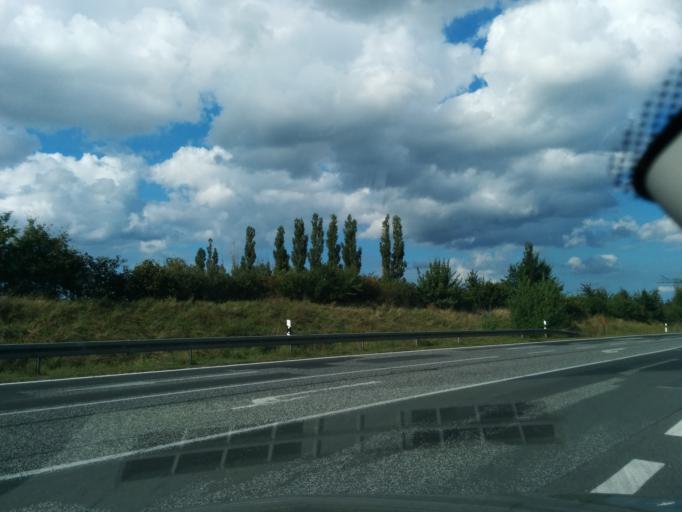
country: DE
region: Mecklenburg-Vorpommern
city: Pasewalk
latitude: 53.4646
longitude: 13.9657
